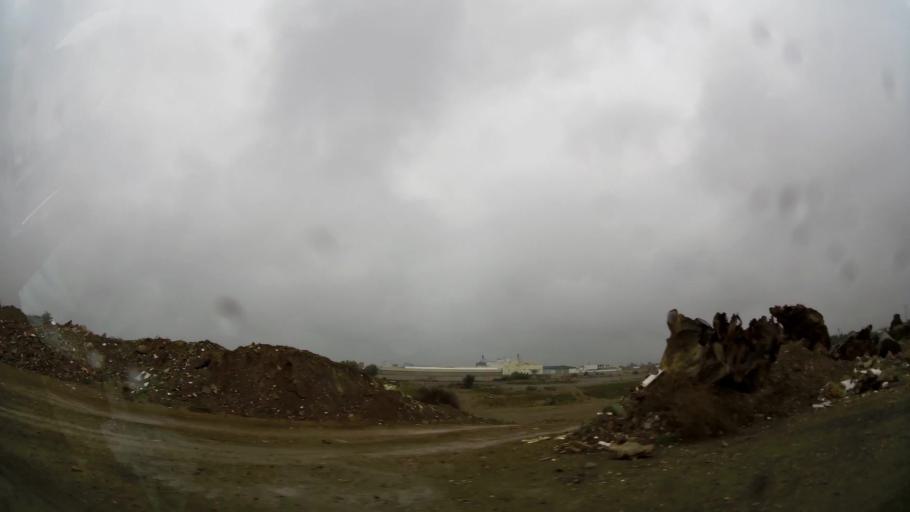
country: MA
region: Taza-Al Hoceima-Taounate
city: Imzourene
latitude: 35.1530
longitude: -3.8200
